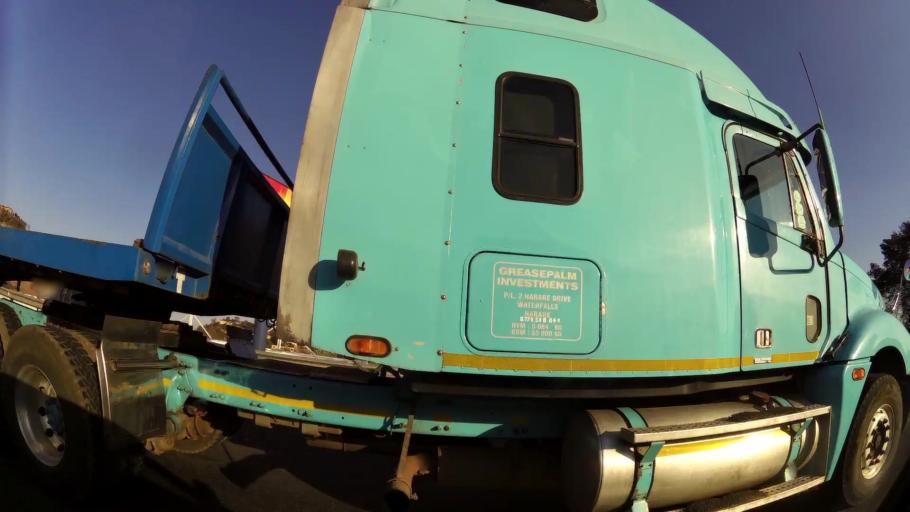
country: ZA
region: Gauteng
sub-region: City of Johannesburg Metropolitan Municipality
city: Johannesburg
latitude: -26.2712
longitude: 28.0444
